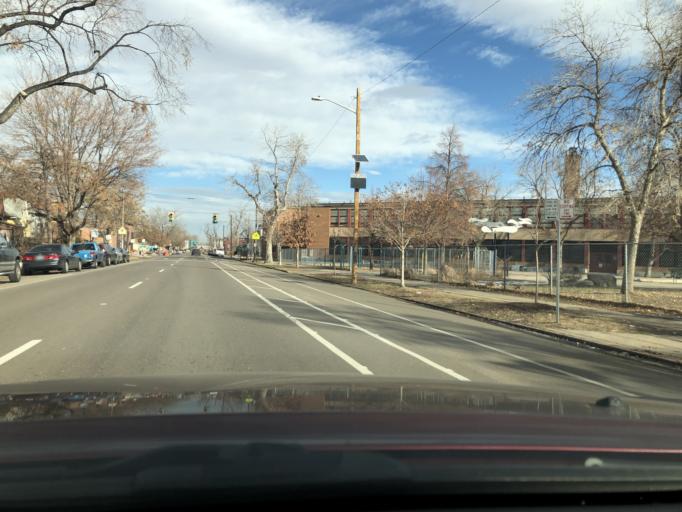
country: US
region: Colorado
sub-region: Denver County
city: Denver
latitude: 39.7582
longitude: -104.9771
